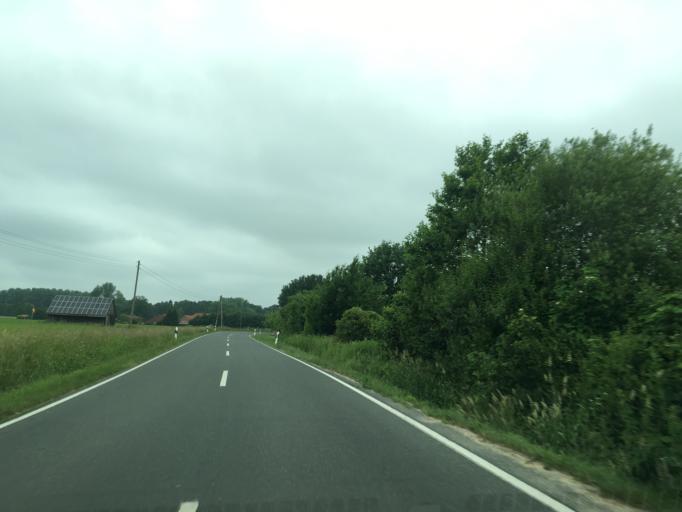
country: DE
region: North Rhine-Westphalia
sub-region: Regierungsbezirk Munster
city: Laer
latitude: 52.0788
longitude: 7.3487
